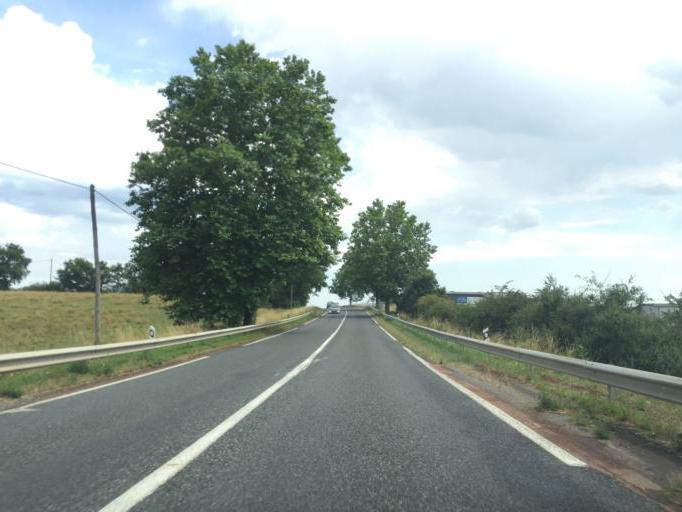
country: FR
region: Rhone-Alpes
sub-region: Departement du Rhone
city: Saint-Romain-de-Popey
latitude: 45.8695
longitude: 4.5421
